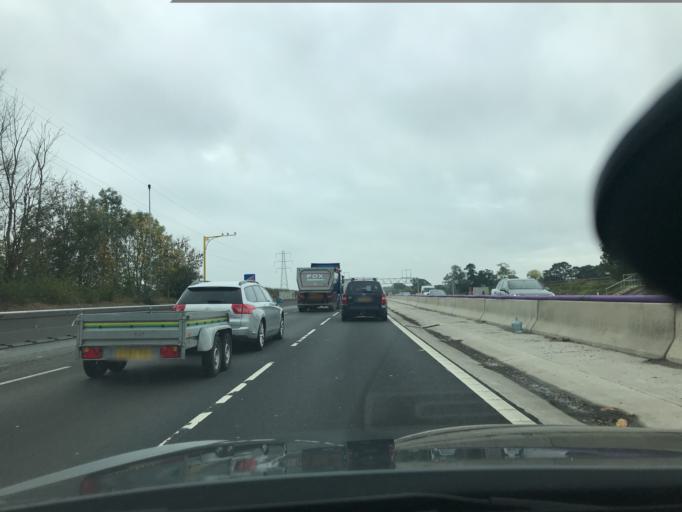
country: GB
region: England
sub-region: Cheshire East
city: Knutsford
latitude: 53.2818
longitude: -2.3954
